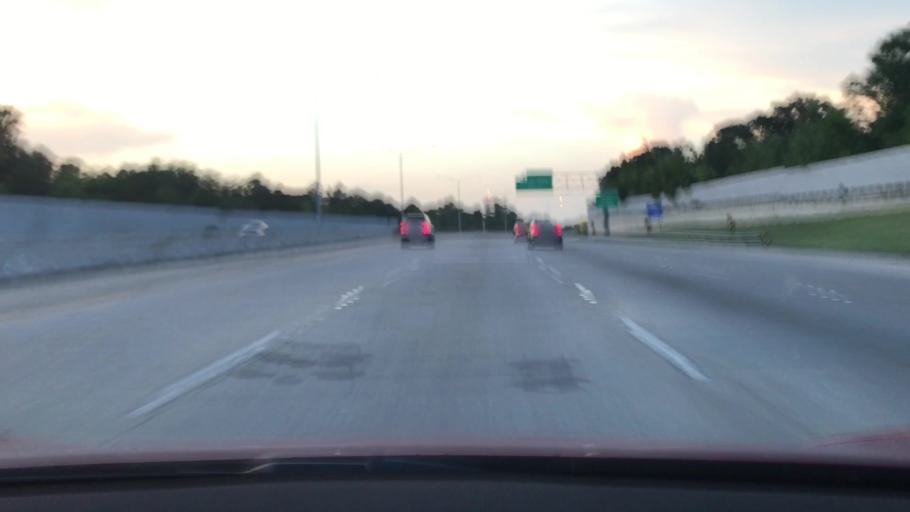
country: US
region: Louisiana
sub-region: Bossier Parish
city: Bossier City
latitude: 32.4606
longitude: -93.7565
